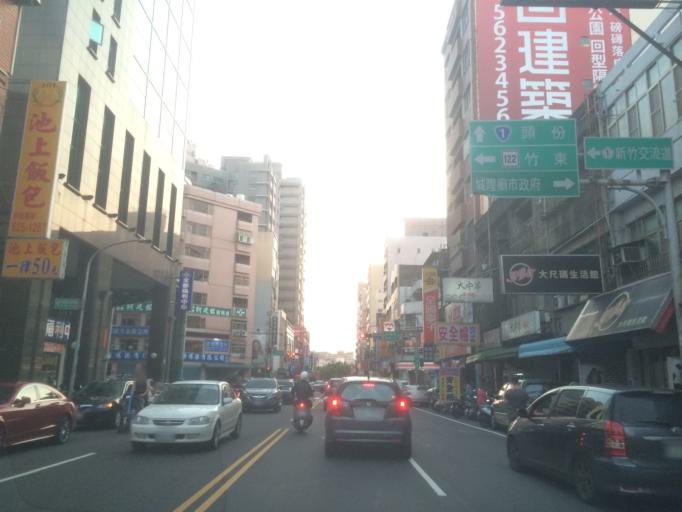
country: TW
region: Taiwan
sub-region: Hsinchu
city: Hsinchu
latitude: 24.7986
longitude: 120.9635
